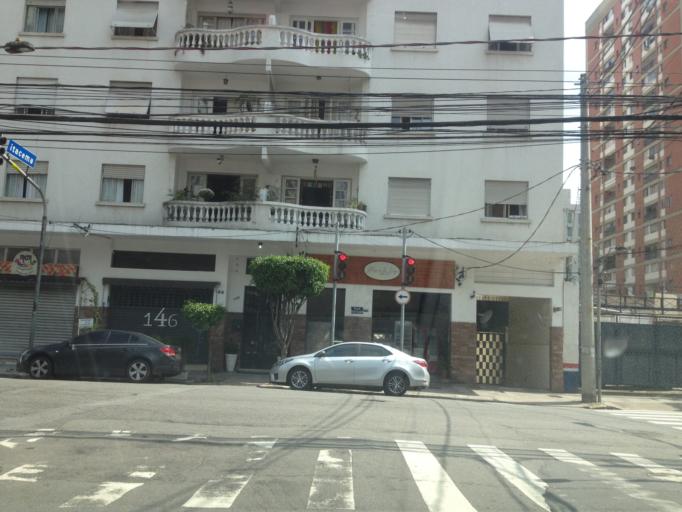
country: BR
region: Sao Paulo
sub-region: Sao Paulo
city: Sao Paulo
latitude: -23.5798
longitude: -46.6747
